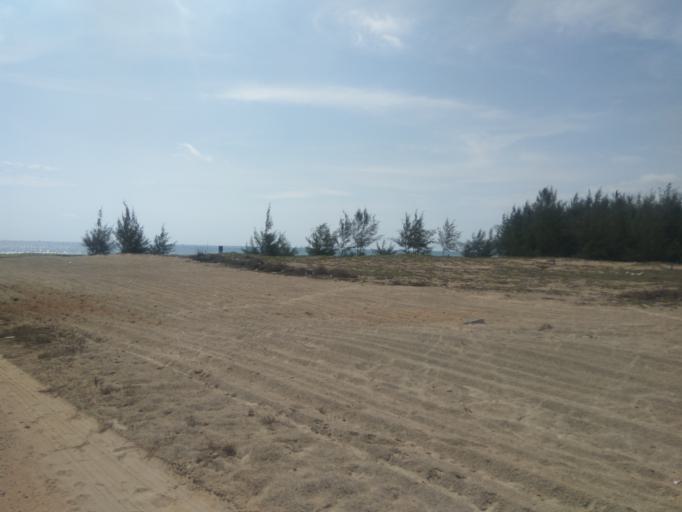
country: IN
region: Tamil Nadu
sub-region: Cuddalore
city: Alappakkam
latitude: 11.5677
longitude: 79.7570
